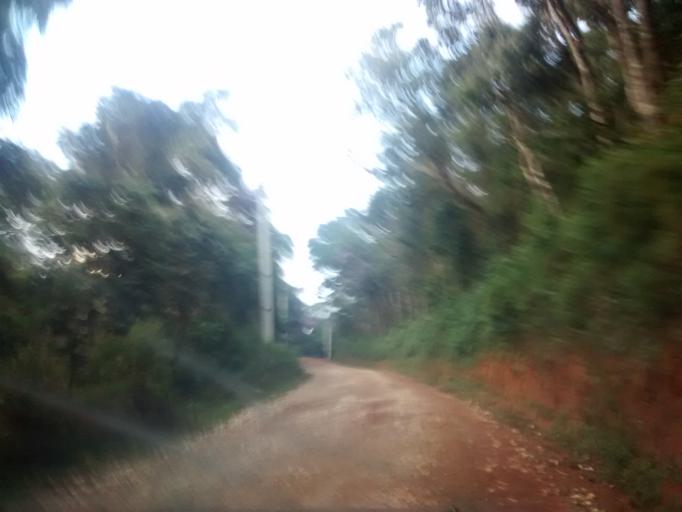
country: BR
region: Sao Paulo
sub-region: Campos Do Jordao
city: Campos do Jordao
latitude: -22.6823
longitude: -45.6369
